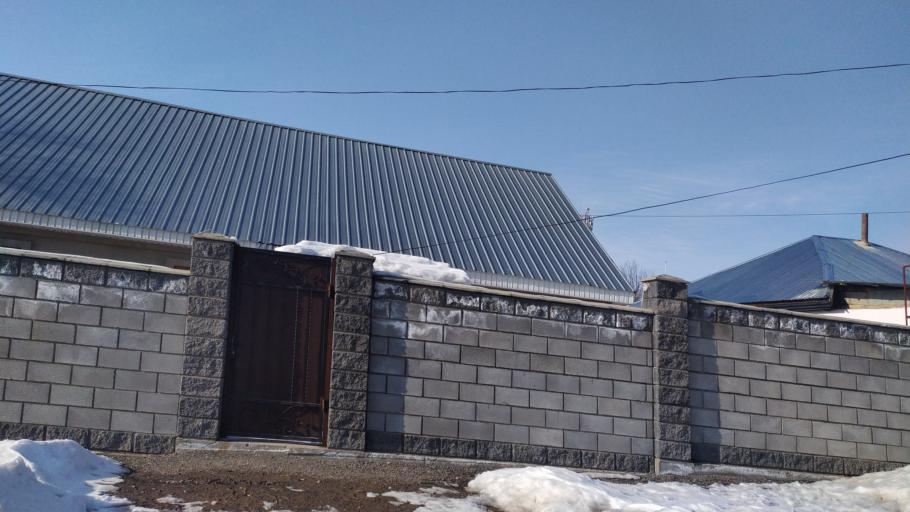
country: KZ
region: Almaty Oblysy
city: Burunday
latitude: 43.2435
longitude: 76.4315
